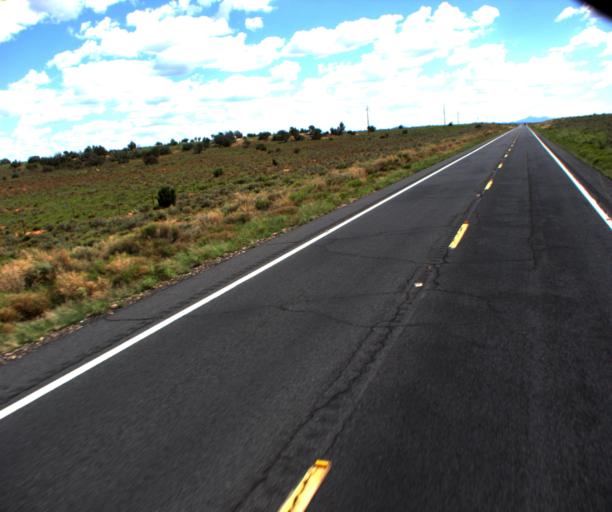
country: US
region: Arizona
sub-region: Coconino County
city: Williams
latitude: 35.6350
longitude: -112.1418
